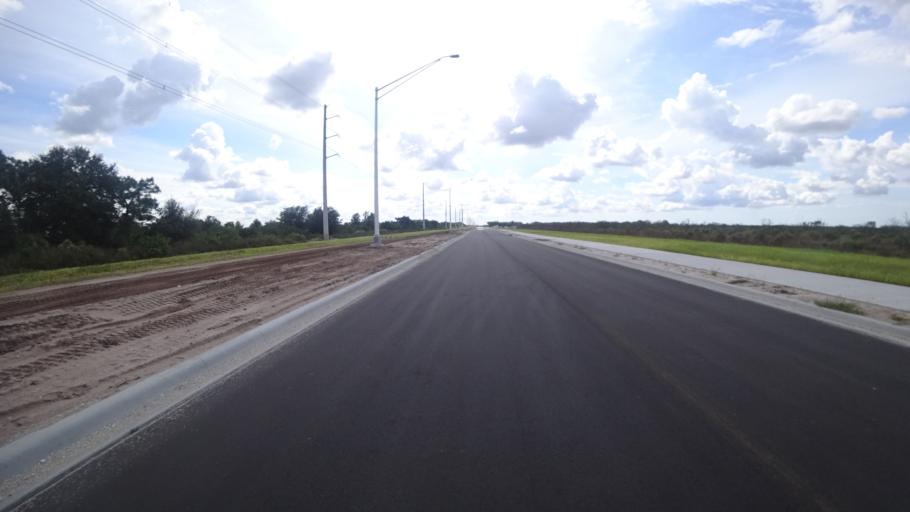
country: US
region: Florida
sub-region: Sarasota County
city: The Meadows
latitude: 27.4649
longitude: -82.3509
